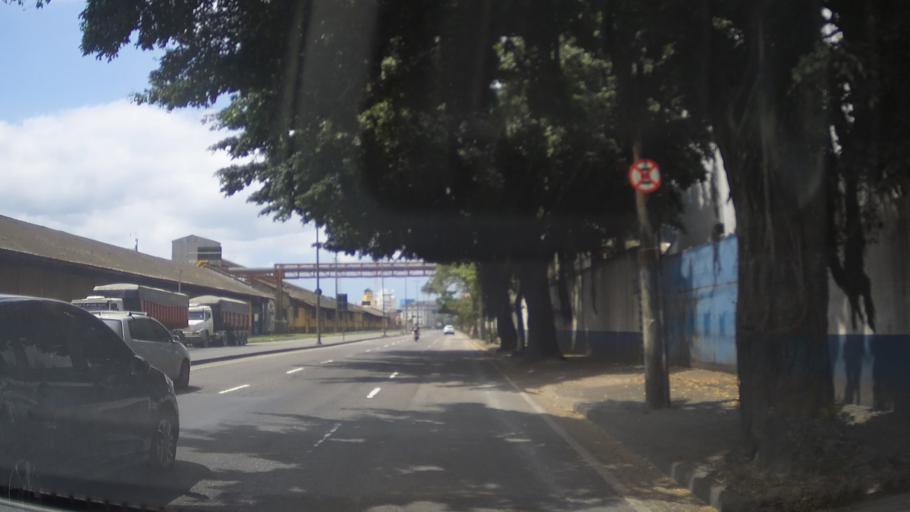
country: BR
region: Sao Paulo
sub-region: Santos
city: Santos
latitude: -23.9332
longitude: -46.3201
